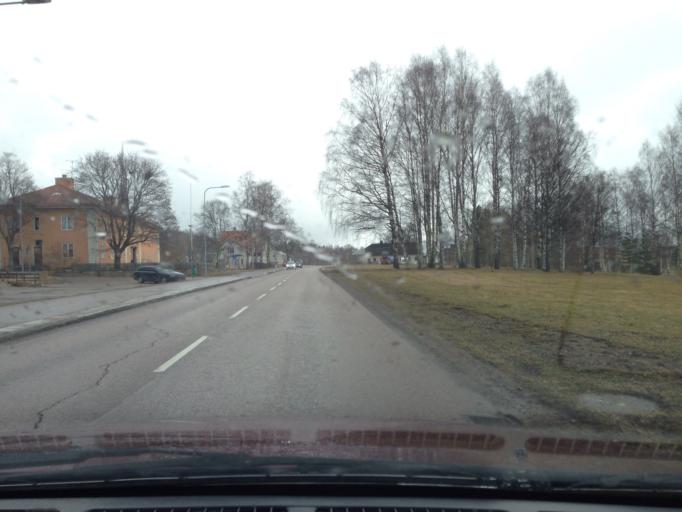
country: SE
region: Dalarna
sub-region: Smedjebackens Kommun
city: Smedjebacken
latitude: 60.1477
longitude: 15.3778
